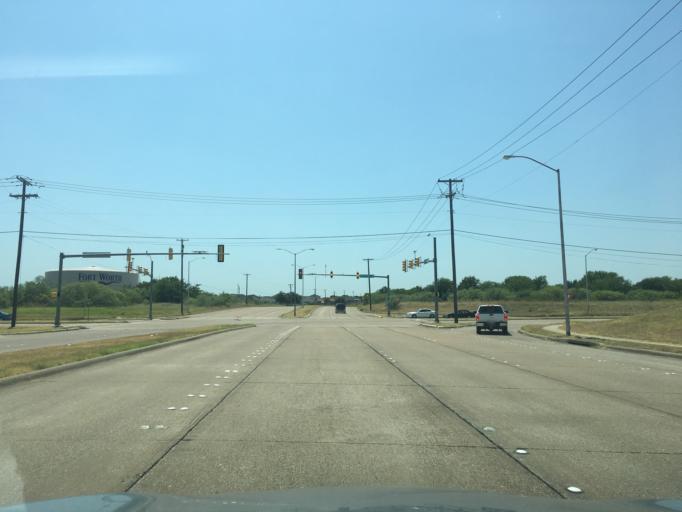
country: US
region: Texas
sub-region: Tarrant County
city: Crowley
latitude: 32.6157
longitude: -97.3712
